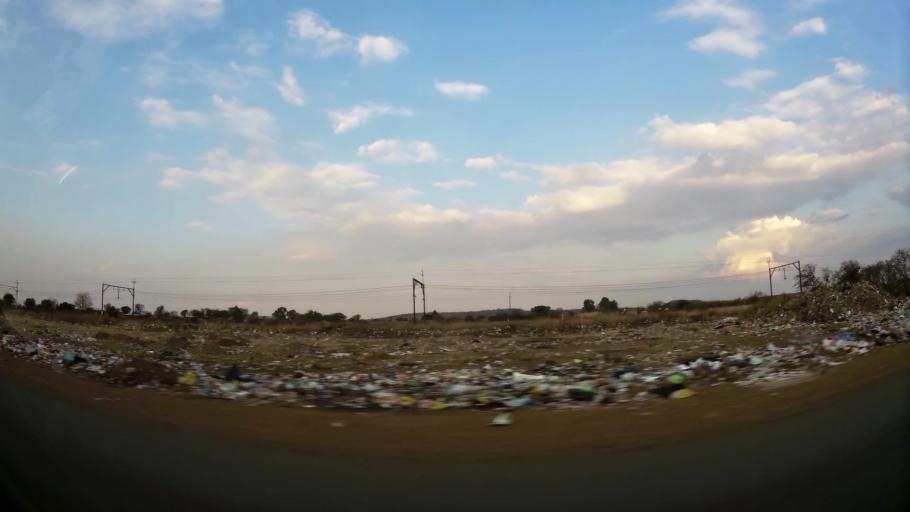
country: ZA
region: Gauteng
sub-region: City of Johannesburg Metropolitan Municipality
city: Orange Farm
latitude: -26.5742
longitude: 27.8586
